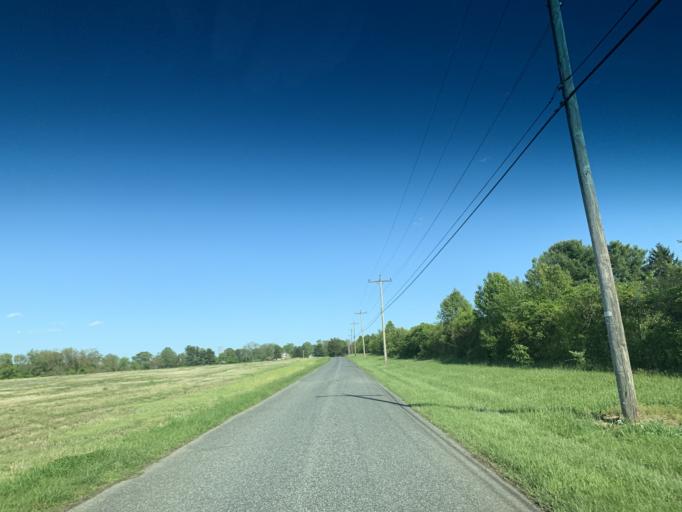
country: US
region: Maryland
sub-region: Harford County
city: Aberdeen
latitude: 39.5017
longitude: -76.1437
